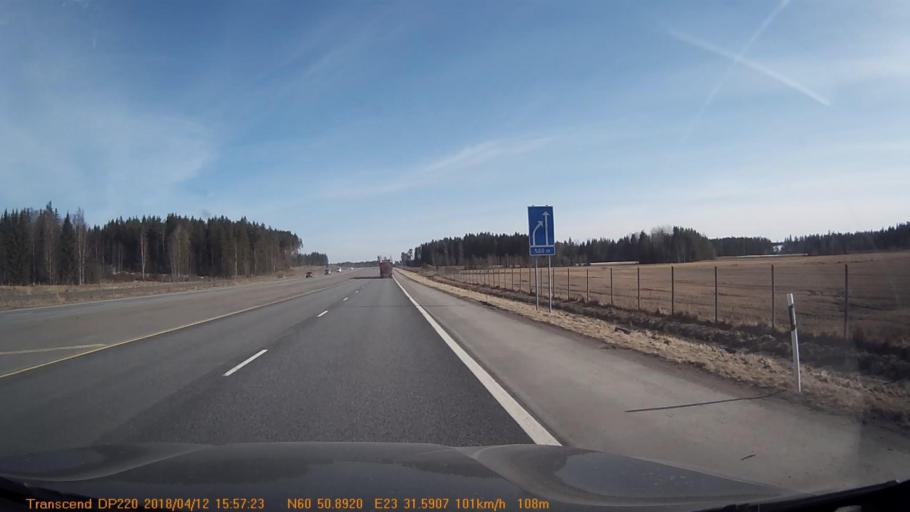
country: FI
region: Haeme
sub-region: Forssa
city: Jokioinen
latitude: 60.8481
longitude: 23.5266
